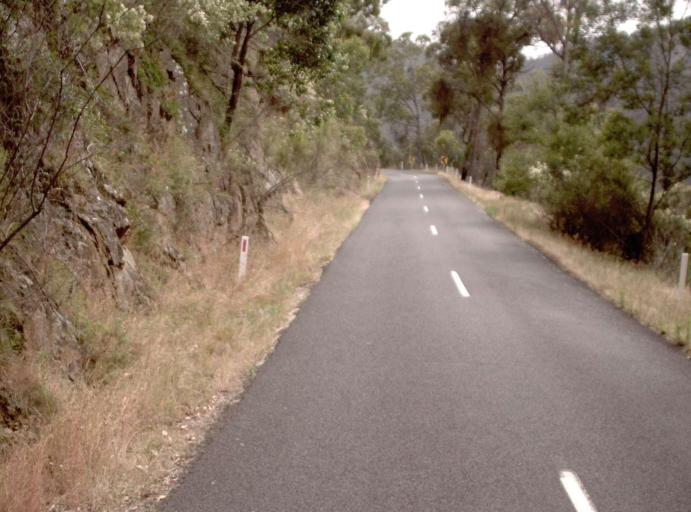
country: AU
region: Victoria
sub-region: Wellington
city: Heyfield
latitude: -37.7394
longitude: 146.6696
